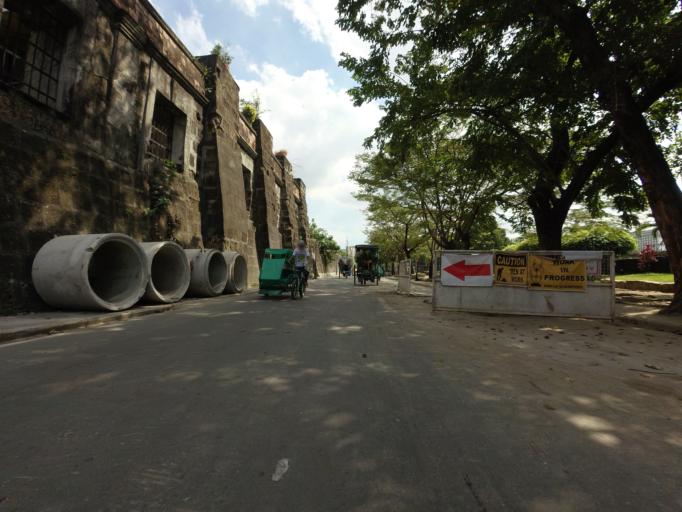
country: PH
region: Metro Manila
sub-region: City of Manila
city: Port Area
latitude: 14.5883
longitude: 120.9740
